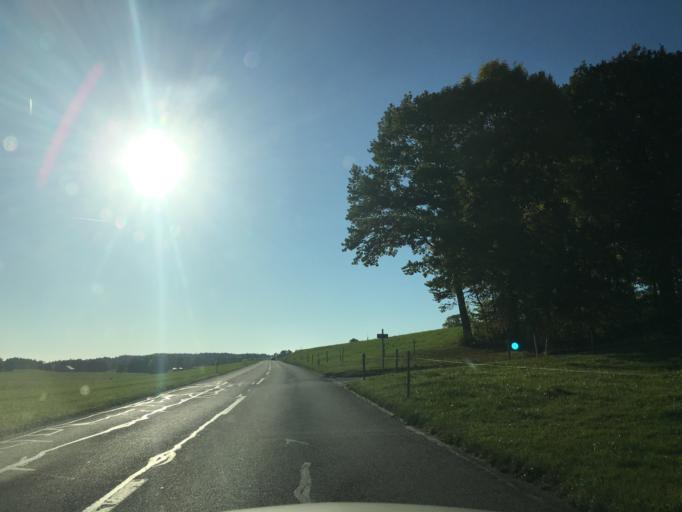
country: CH
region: Fribourg
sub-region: Gruyere District
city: Sales
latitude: 46.6119
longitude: 6.9270
